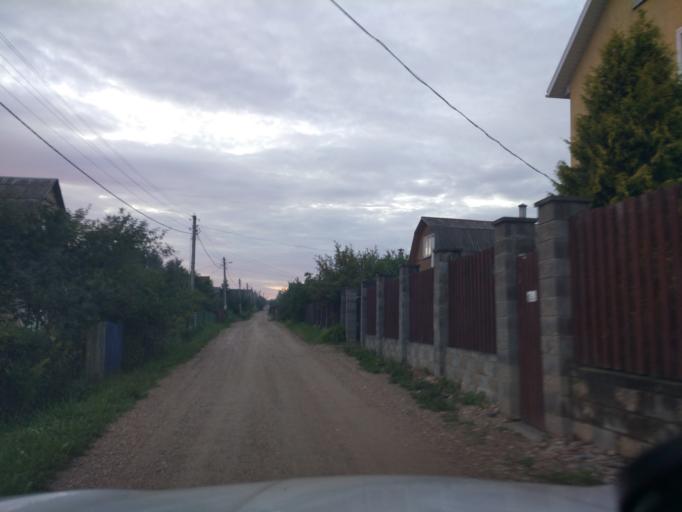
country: BY
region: Minsk
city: Astrashytski Haradok
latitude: 54.0863
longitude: 27.7002
